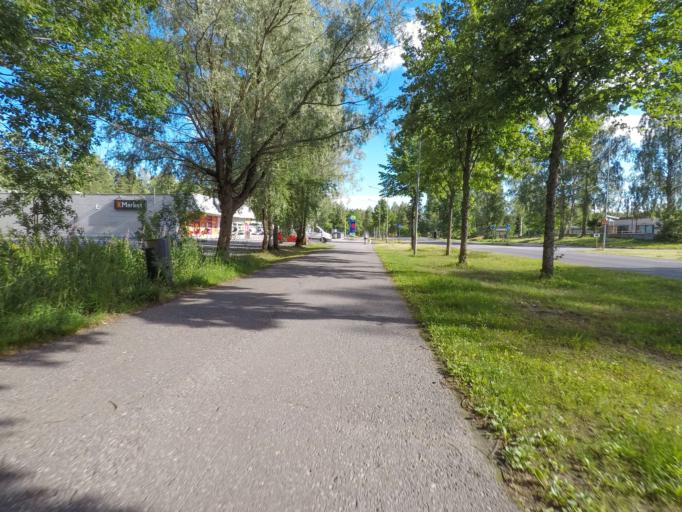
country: FI
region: South Karelia
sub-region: Lappeenranta
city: Lappeenranta
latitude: 61.0783
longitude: 28.1502
